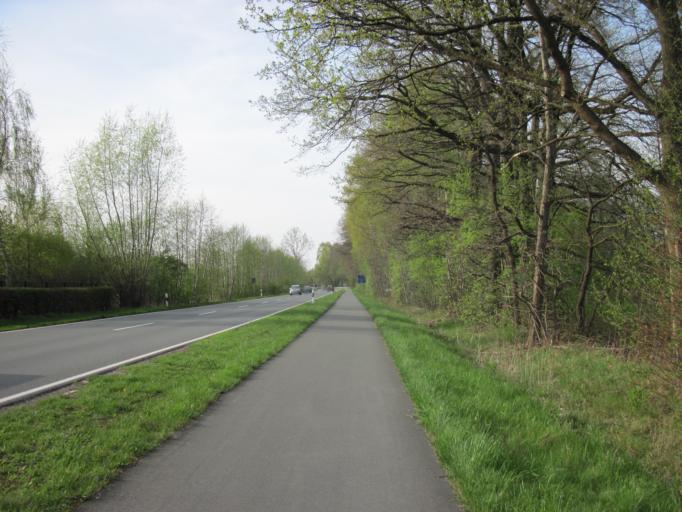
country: DE
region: North Rhine-Westphalia
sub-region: Regierungsbezirk Detmold
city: Hovelhof
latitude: 51.7834
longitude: 8.7083
